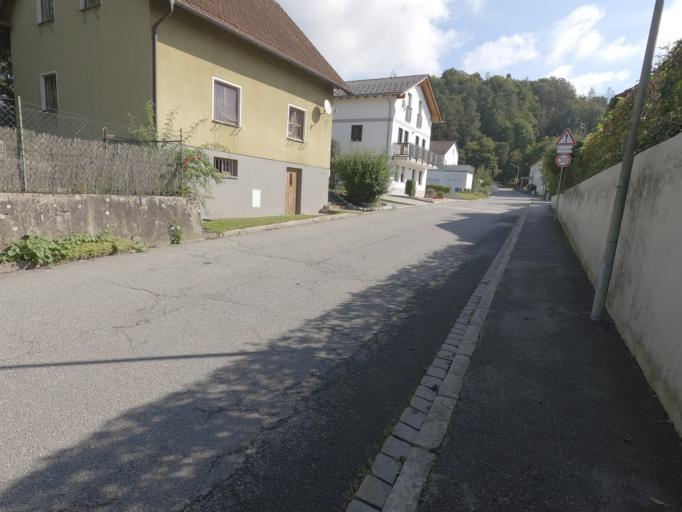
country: DE
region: Bavaria
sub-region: Lower Bavaria
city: Niederalteich
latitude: 48.7983
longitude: 13.0110
